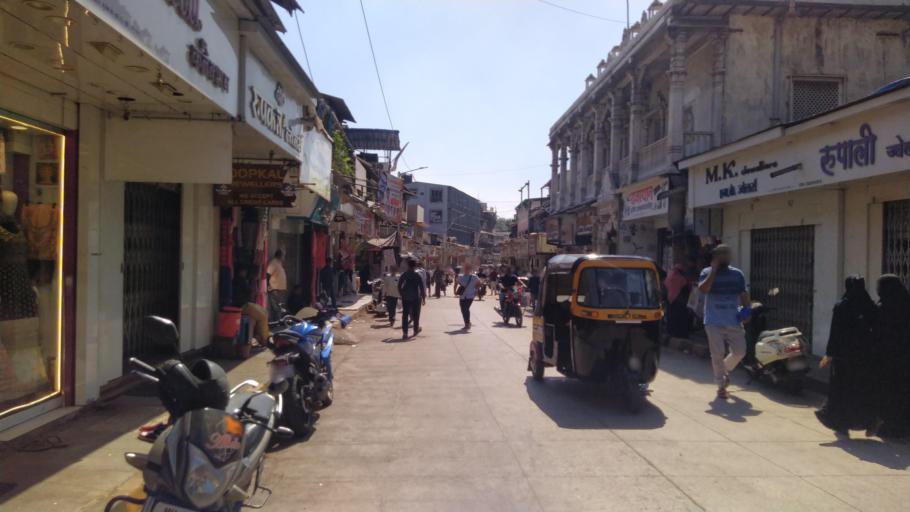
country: IN
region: Maharashtra
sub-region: Mumbai Suburban
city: Mumbai
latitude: 19.0682
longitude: 72.8779
